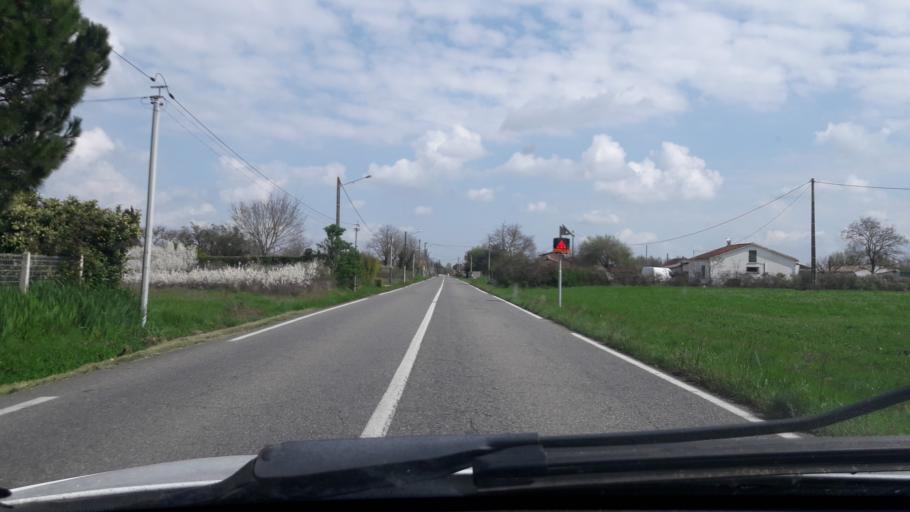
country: FR
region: Midi-Pyrenees
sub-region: Departement de la Haute-Garonne
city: Fonsorbes
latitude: 43.5041
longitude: 1.2514
